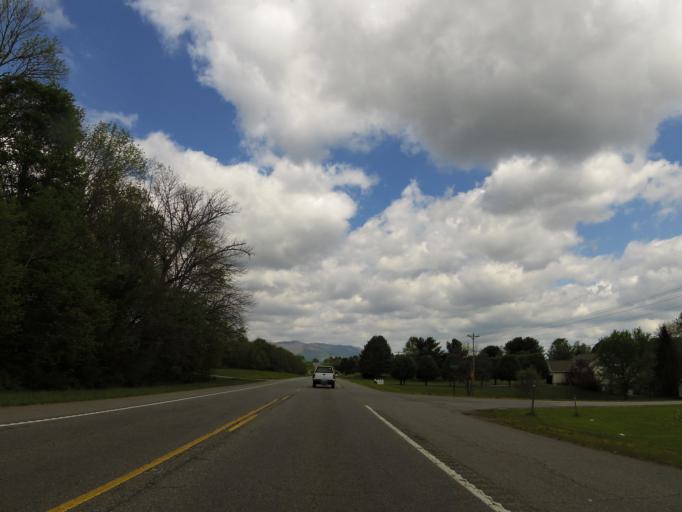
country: US
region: Tennessee
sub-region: Campbell County
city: Fincastle
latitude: 36.4118
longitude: -84.0548
